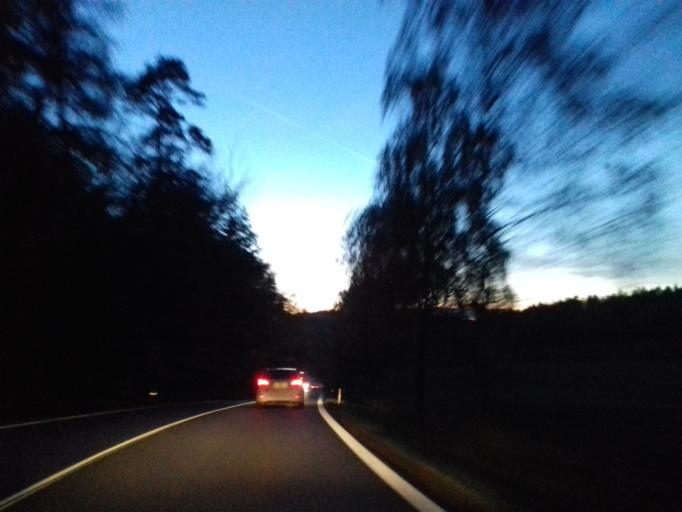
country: CZ
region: Vysocina
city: Vilemov
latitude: 49.5477
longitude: 15.4039
